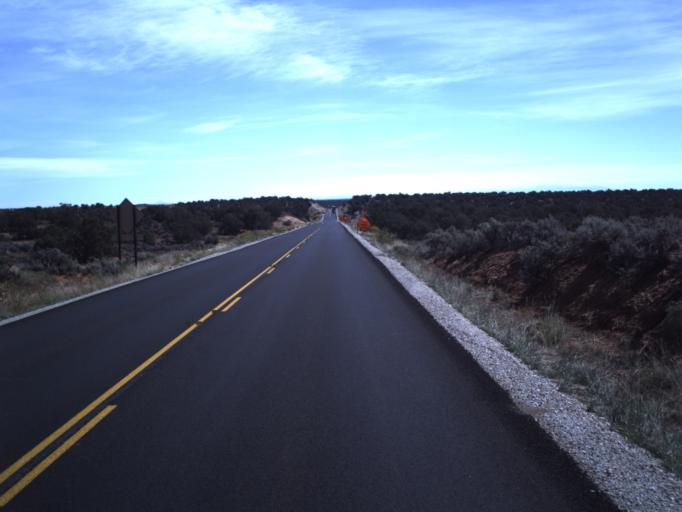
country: US
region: Utah
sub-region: San Juan County
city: Blanding
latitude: 37.5753
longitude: -109.5383
